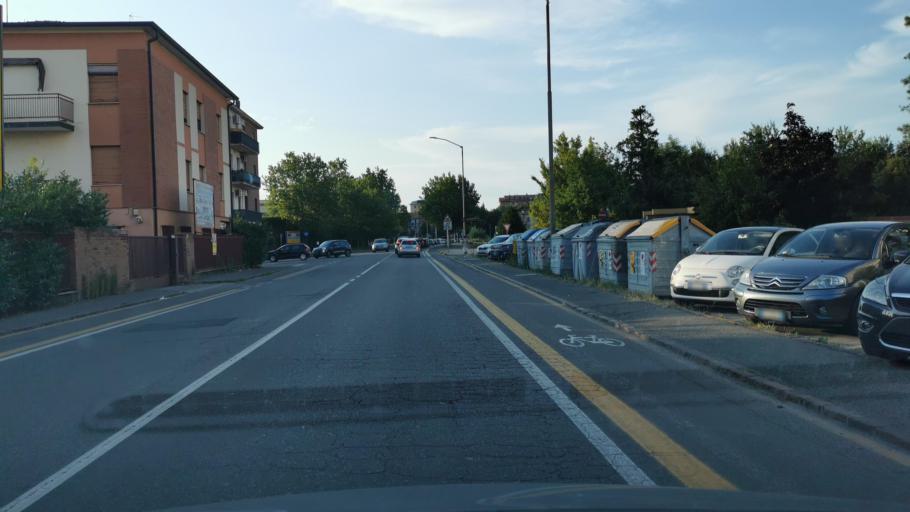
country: IT
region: Emilia-Romagna
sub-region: Provincia di Modena
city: Modena
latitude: 44.6305
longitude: 10.9266
